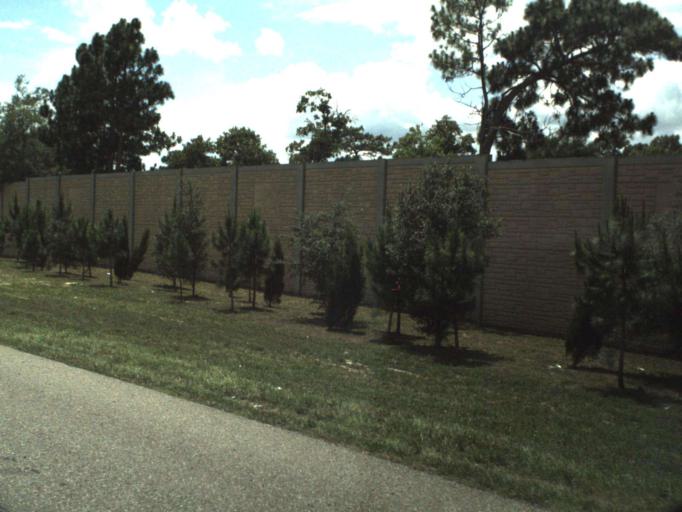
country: US
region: Florida
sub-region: Volusia County
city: Orange City
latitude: 28.9419
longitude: -81.2621
